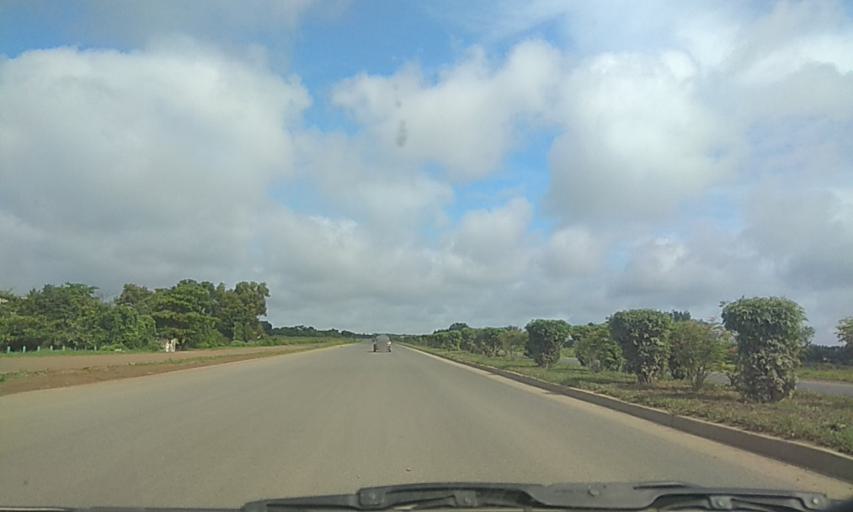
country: IN
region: Karnataka
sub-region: Haveri
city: Shiggaon
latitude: 14.9975
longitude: 75.2098
